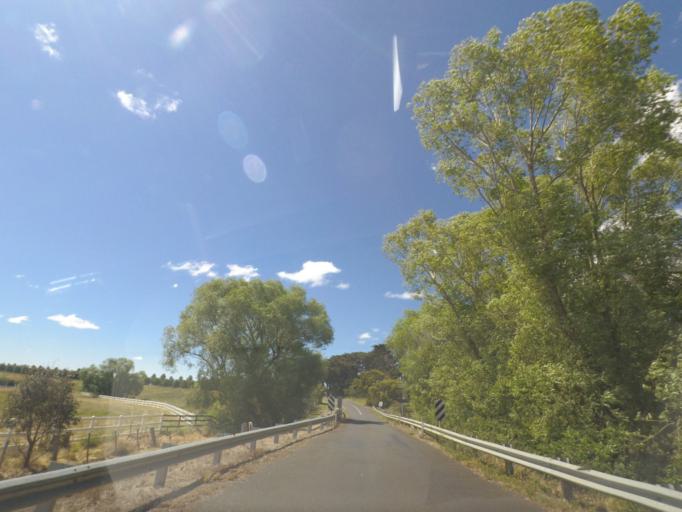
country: AU
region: Victoria
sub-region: Moorabool
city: Bacchus Marsh
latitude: -37.3302
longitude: 144.4433
